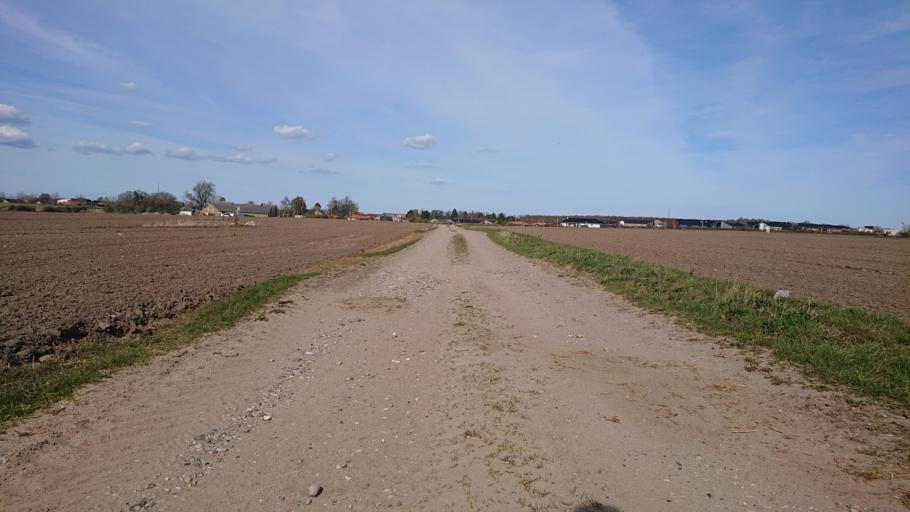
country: DK
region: South Denmark
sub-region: Nyborg Kommune
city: Nyborg
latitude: 55.3032
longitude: 10.7485
